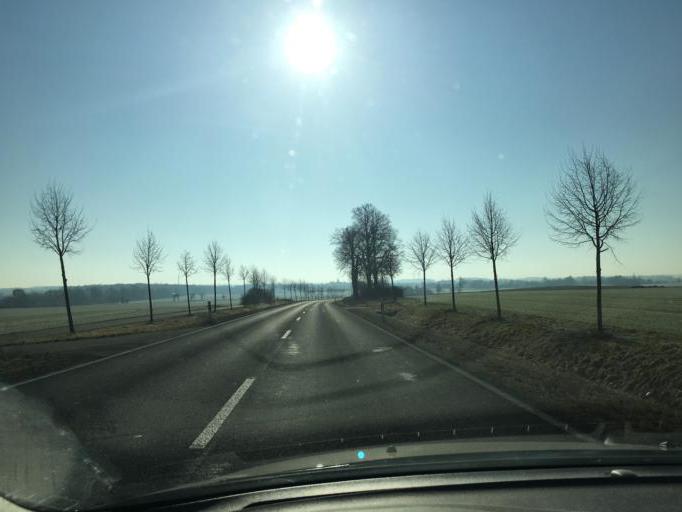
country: DE
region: Saxony
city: Bad Lausick
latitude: 51.1652
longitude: 12.6271
